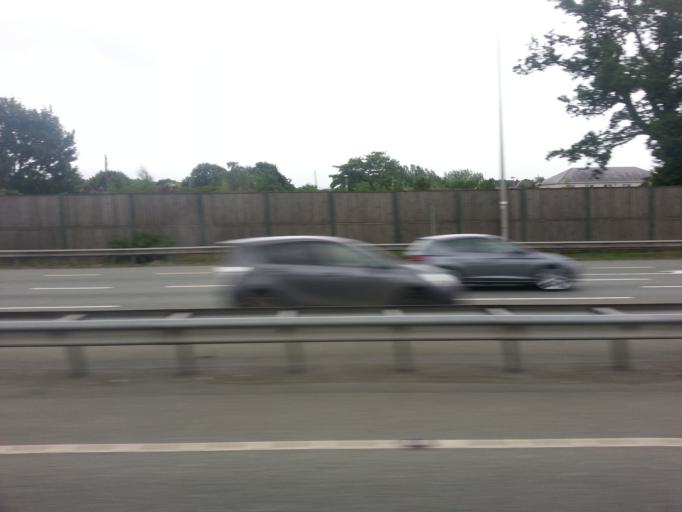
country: IE
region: Leinster
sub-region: Kildare
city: Johnstown
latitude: 53.2369
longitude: -6.6243
